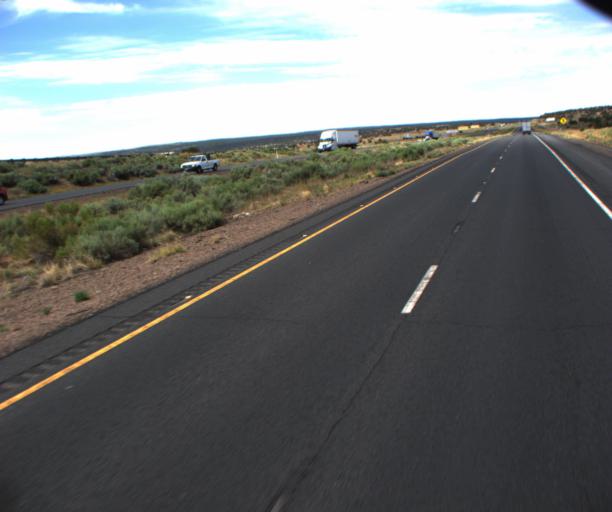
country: US
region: Arizona
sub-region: Apache County
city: Houck
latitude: 35.2884
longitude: -109.1584
